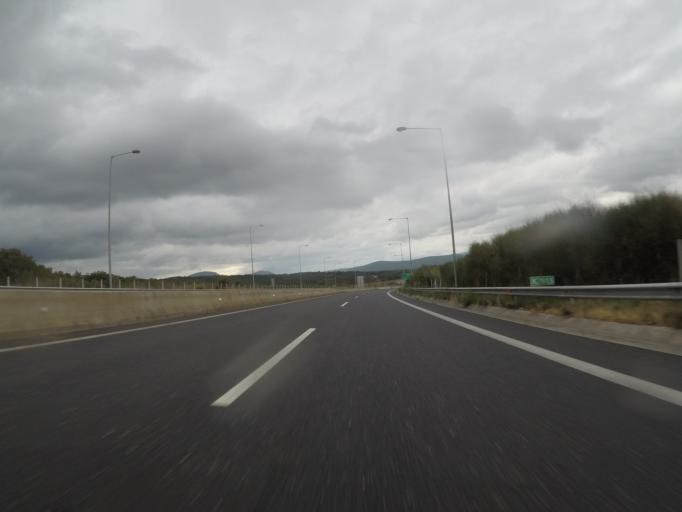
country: GR
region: Peloponnese
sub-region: Nomos Arkadias
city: Megalopoli
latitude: 37.3598
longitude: 22.1460
